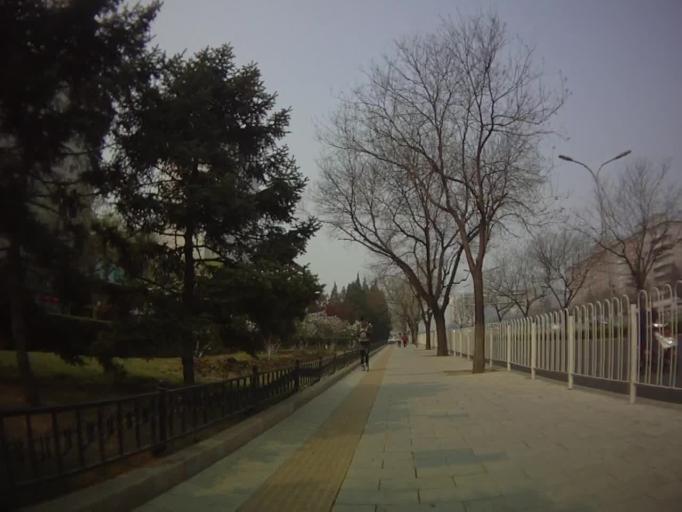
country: CN
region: Beijing
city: Chaowai
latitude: 39.9069
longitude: 116.4340
